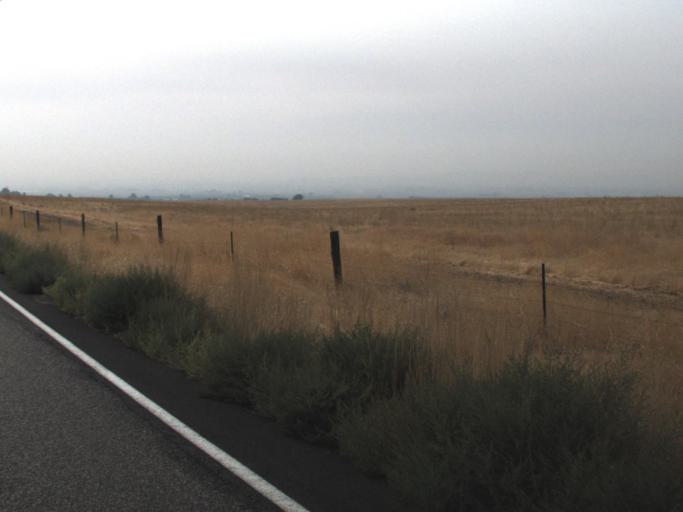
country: US
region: Washington
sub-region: Yakima County
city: Sunnyside
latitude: 46.4099
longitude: -119.9486
